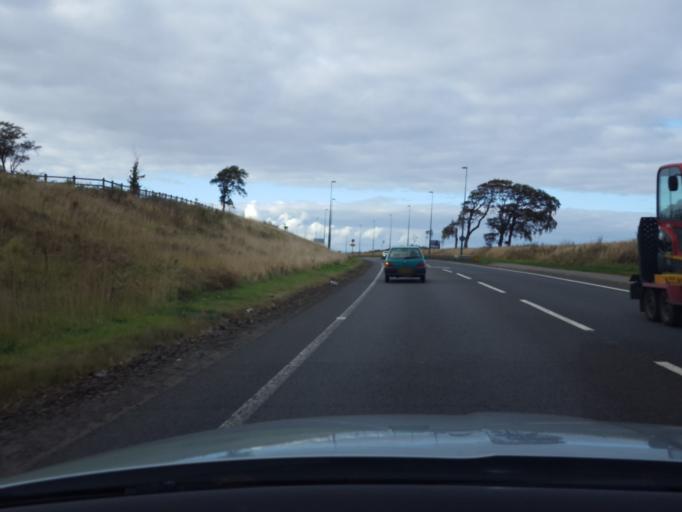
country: GB
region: Scotland
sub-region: Fife
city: Pathhead
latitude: 55.8903
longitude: -2.9963
